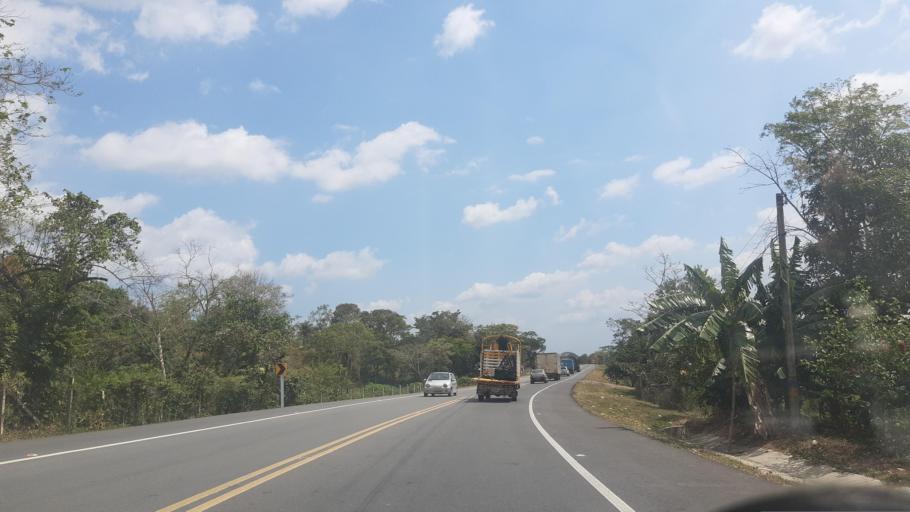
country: CO
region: Casanare
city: Tauramena
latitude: 5.0210
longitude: -72.6645
